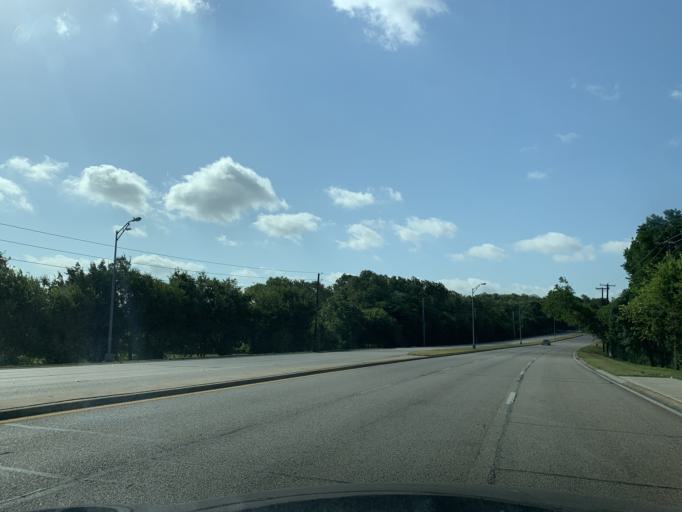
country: US
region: Texas
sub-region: Dallas County
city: Hutchins
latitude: 32.6793
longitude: -96.7858
